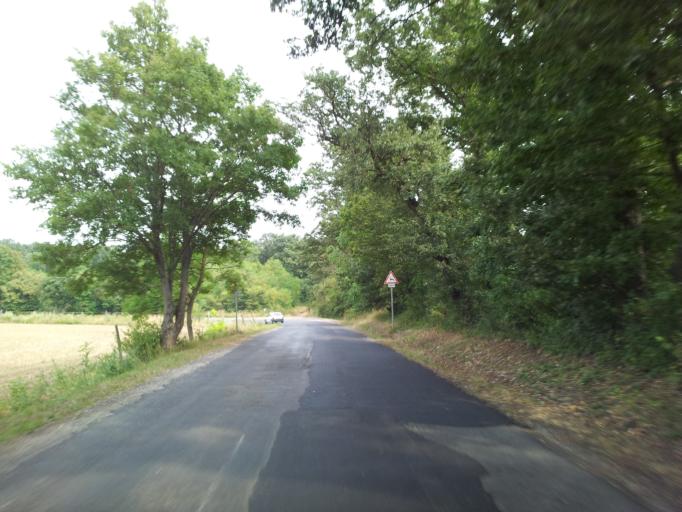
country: HU
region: Veszprem
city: Balatonfured
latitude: 46.9373
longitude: 17.8030
